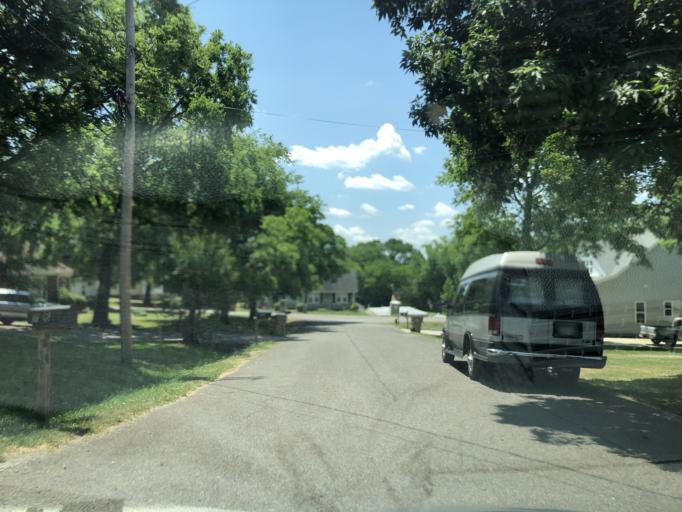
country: US
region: Tennessee
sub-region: Davidson County
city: Goodlettsville
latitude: 36.2705
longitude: -86.7066
